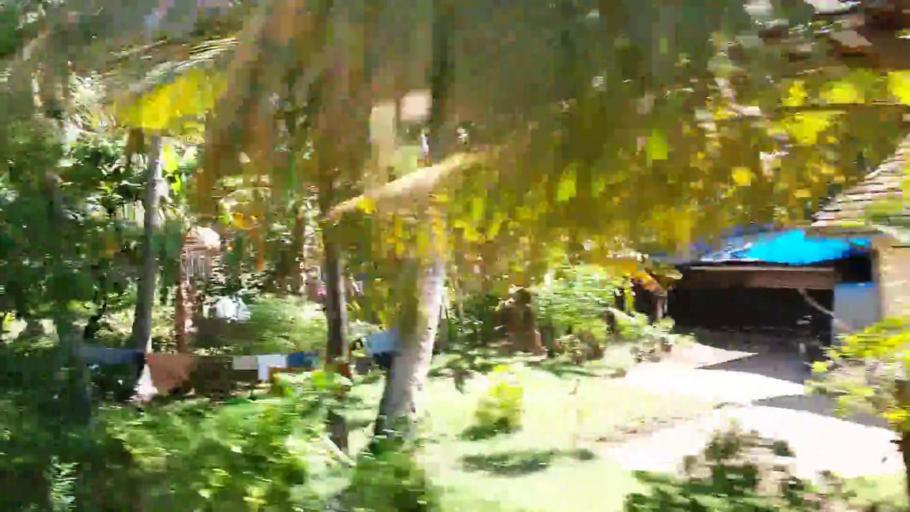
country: LK
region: Southern
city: Hikkaduwa
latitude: 6.1624
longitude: 80.0928
